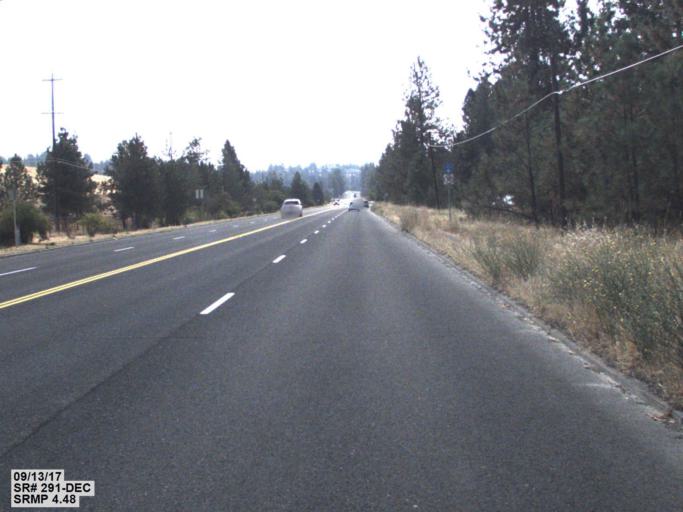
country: US
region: Washington
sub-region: Spokane County
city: Town and Country
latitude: 47.7286
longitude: -117.4991
